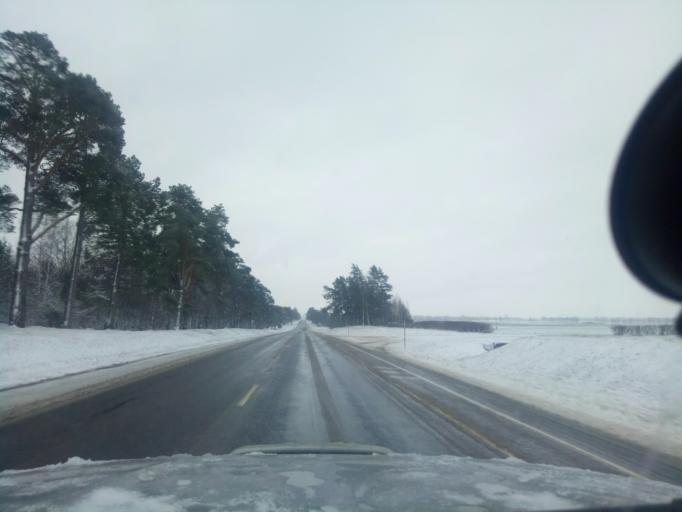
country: BY
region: Minsk
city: Nyasvizh
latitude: 53.2591
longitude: 26.6121
